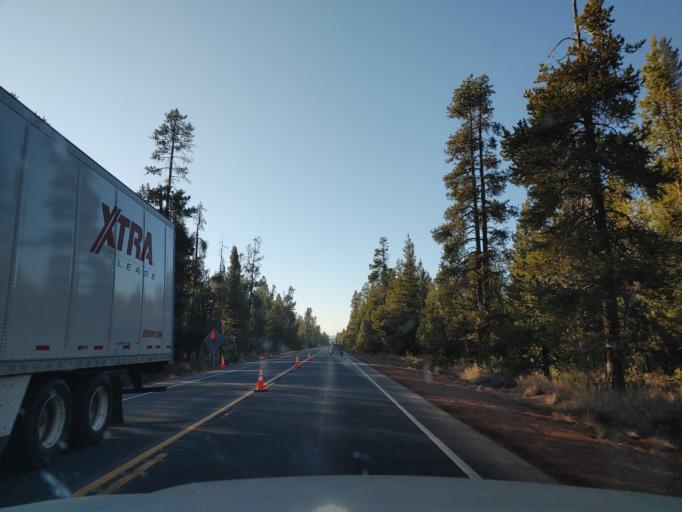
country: US
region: Oregon
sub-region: Deschutes County
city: La Pine
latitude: 43.3836
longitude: -121.8043
